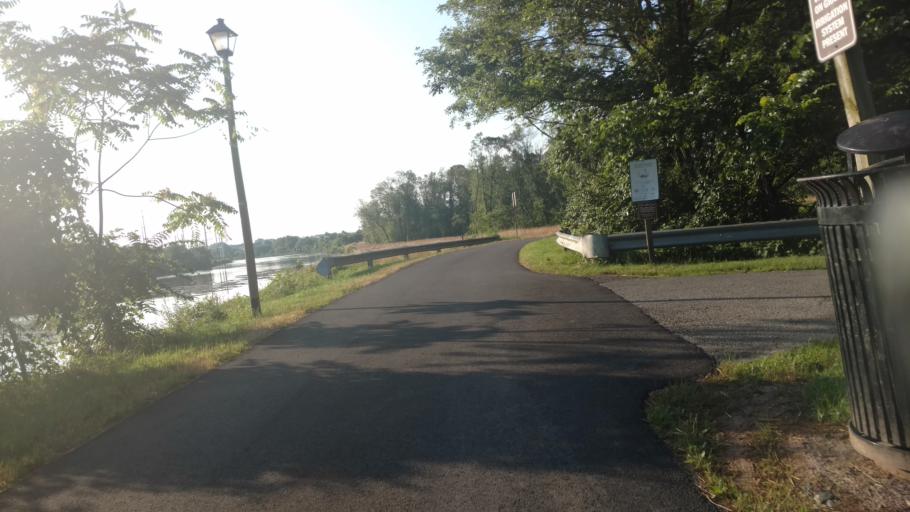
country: US
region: Virginia
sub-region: City of Alexandria
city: Alexandria
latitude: 38.8431
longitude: -77.0613
